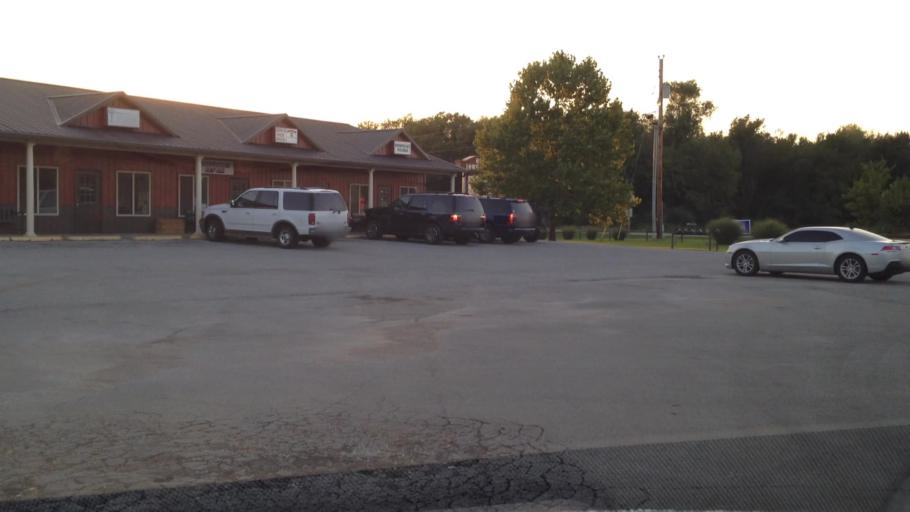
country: US
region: Oklahoma
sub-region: Delaware County
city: Cleora
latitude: 36.5678
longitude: -94.9769
